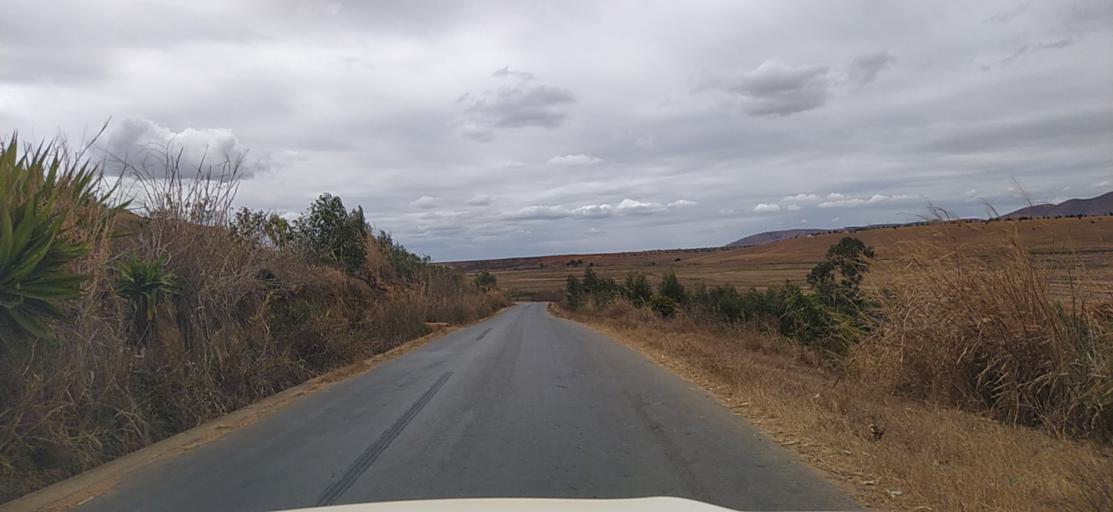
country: MG
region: Alaotra Mangoro
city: Ambatondrazaka
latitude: -17.9271
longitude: 48.2577
